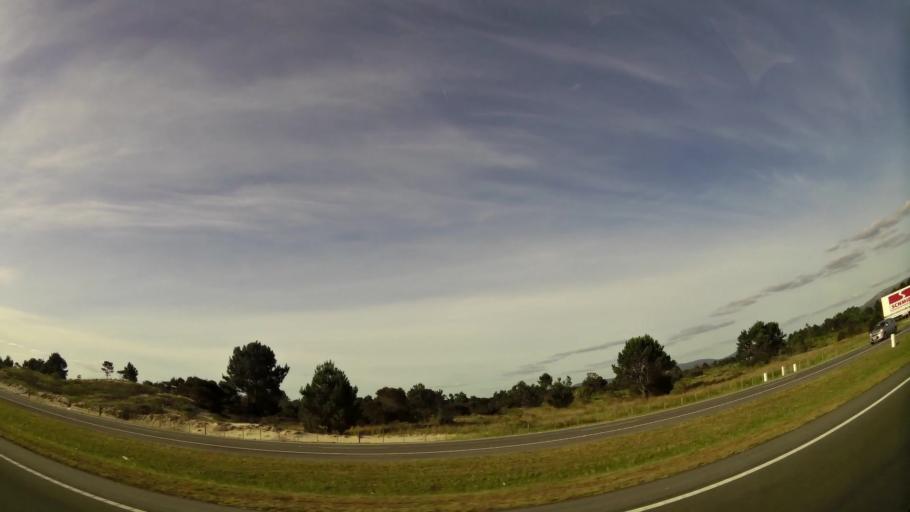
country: UY
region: Maldonado
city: Piriapolis
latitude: -34.7800
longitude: -55.4252
